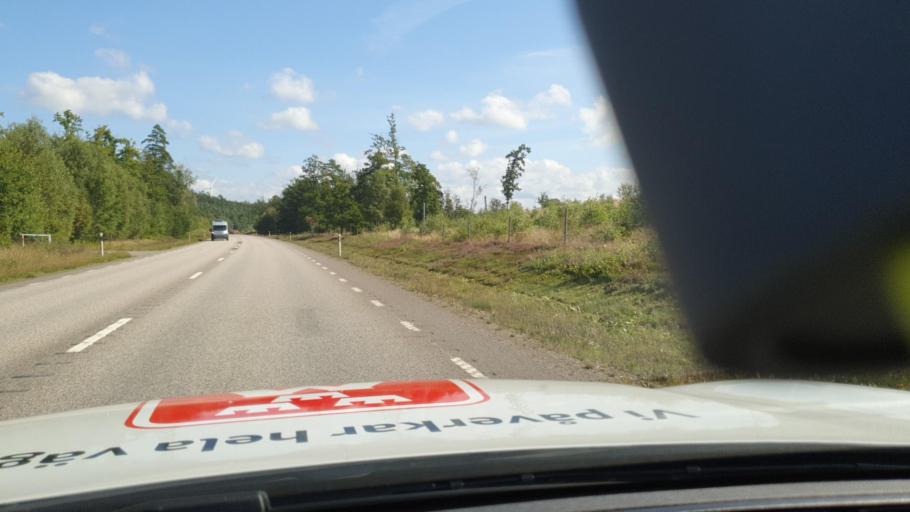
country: SE
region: Halland
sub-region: Laholms Kommun
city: Knared
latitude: 56.5266
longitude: 13.1978
